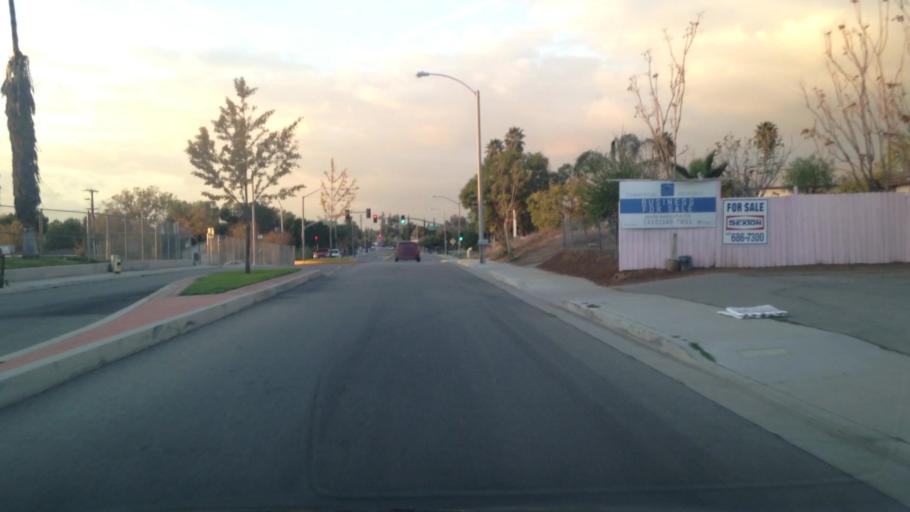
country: US
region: California
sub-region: Riverside County
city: Pedley
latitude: 33.9329
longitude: -117.4770
